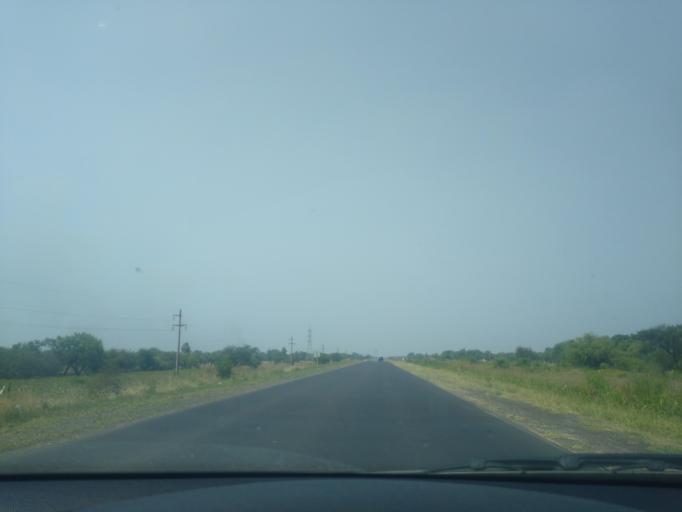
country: AR
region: Chaco
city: Fontana
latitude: -27.4989
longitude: -59.0825
